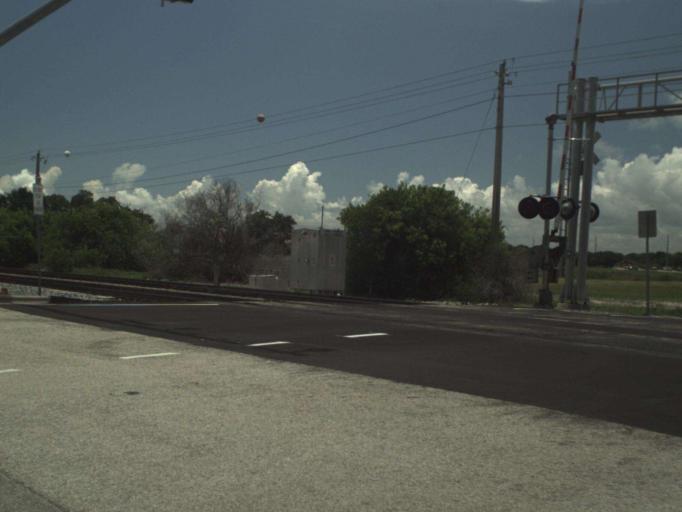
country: US
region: Florida
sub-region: Indian River County
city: Vero Beach
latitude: 27.6516
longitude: -80.4011
